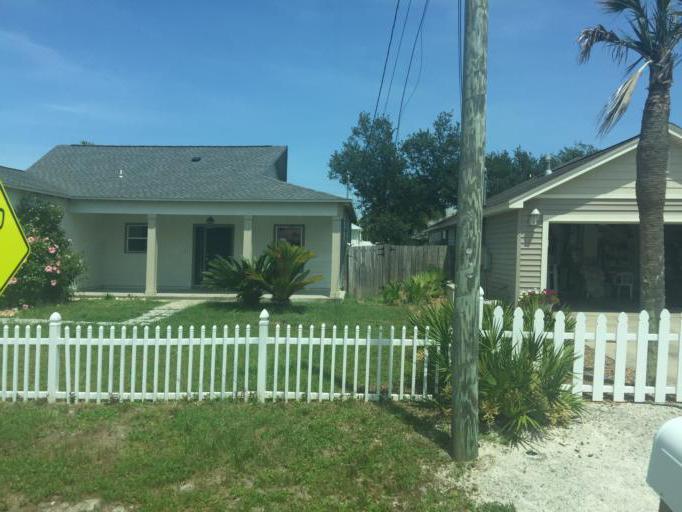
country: US
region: Florida
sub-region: Bay County
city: Laguna Beach
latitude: 30.2386
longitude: -85.9140
